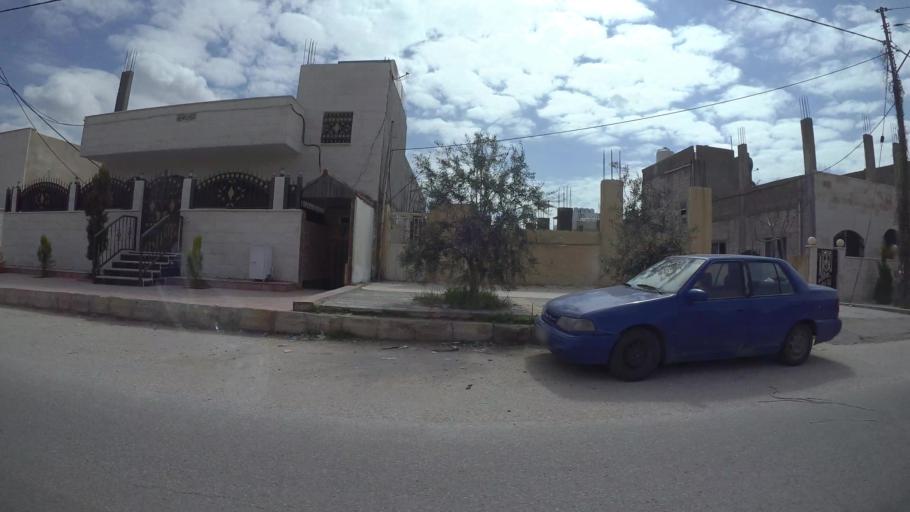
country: JO
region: Amman
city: Al Jubayhah
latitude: 32.0696
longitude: 35.8166
